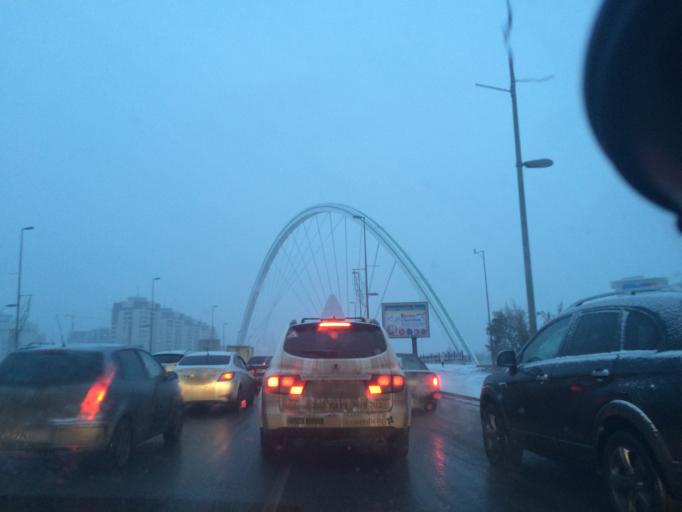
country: KZ
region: Astana Qalasy
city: Astana
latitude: 51.1532
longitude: 71.4299
